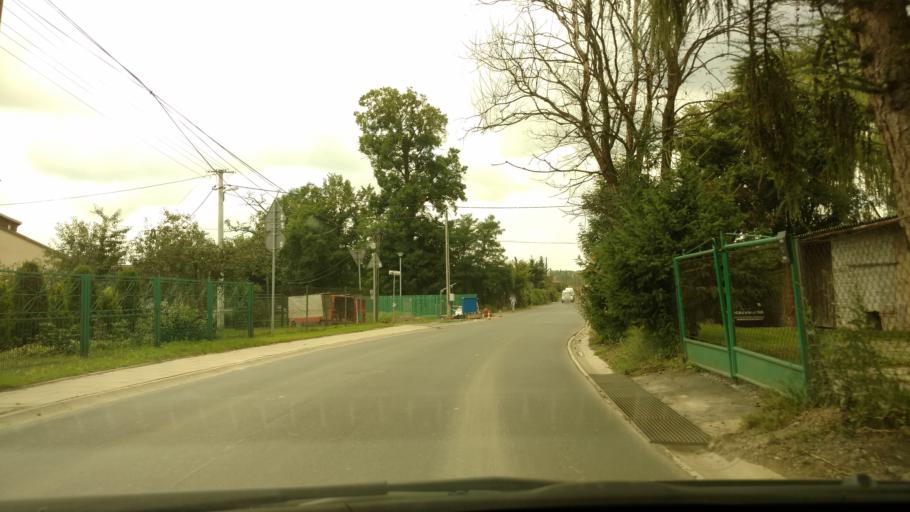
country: PL
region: Lesser Poland Voivodeship
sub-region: Powiat krakowski
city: Zielonki
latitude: 50.1125
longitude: 19.8953
